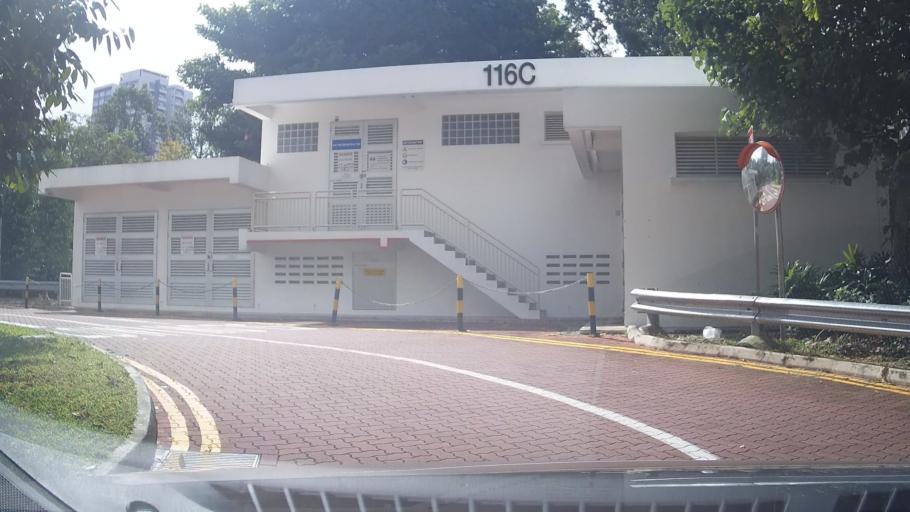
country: SG
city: Singapore
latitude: 1.3268
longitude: 103.8602
